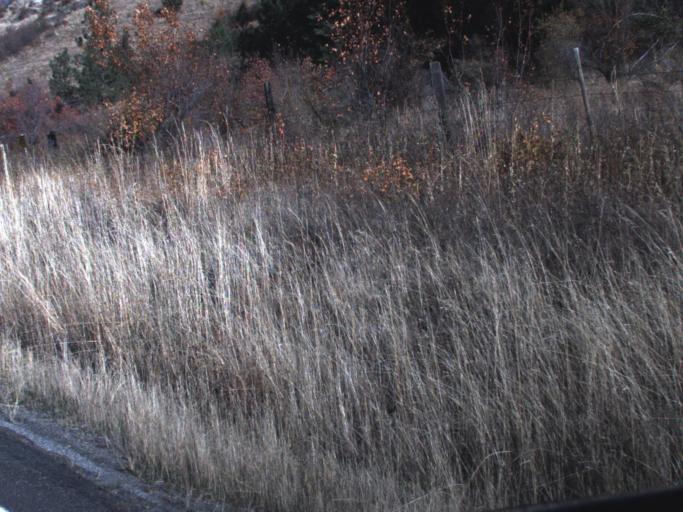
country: US
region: Washington
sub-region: Lincoln County
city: Davenport
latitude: 48.1303
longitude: -118.2059
